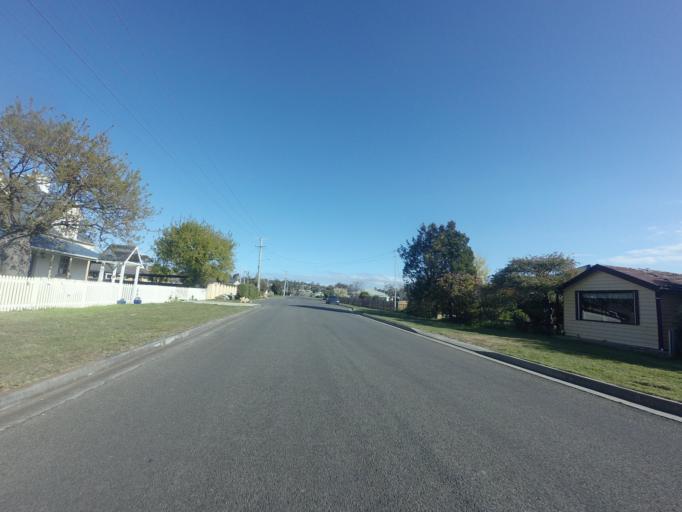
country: AU
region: Tasmania
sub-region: Sorell
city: Sorell
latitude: -42.5065
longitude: 147.9163
